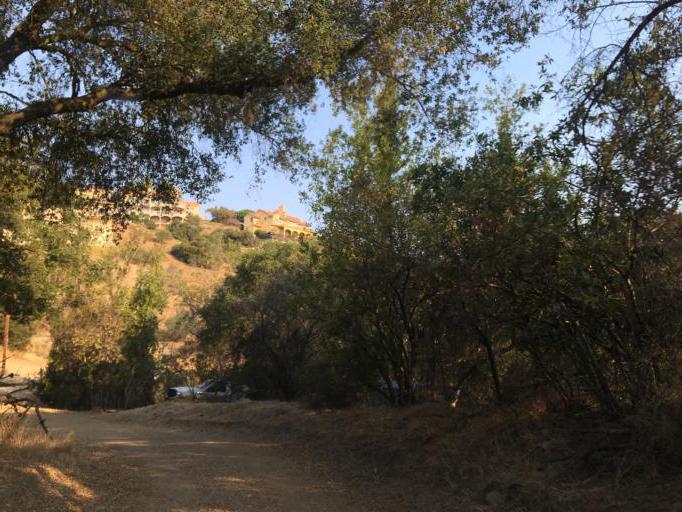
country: US
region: California
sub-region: Los Angeles County
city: Topanga
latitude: 34.0722
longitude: -118.5999
